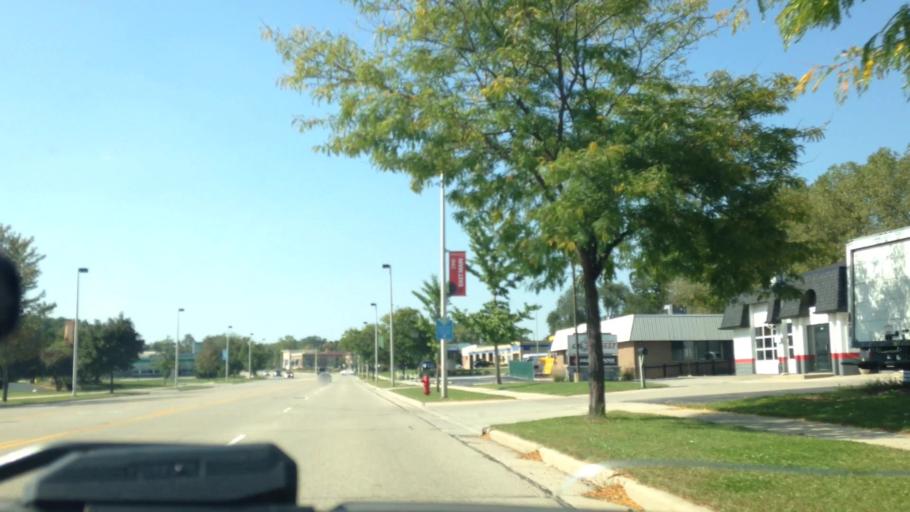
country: US
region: Wisconsin
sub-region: Waukesha County
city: Menomonee Falls
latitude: 43.1782
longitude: -88.0989
